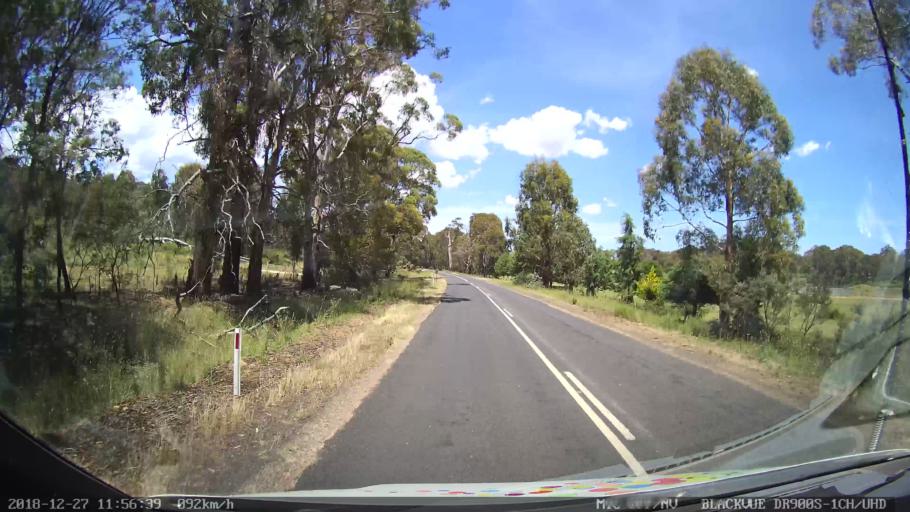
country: AU
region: New South Wales
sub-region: Blayney
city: Blayney
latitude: -33.7009
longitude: 149.3894
